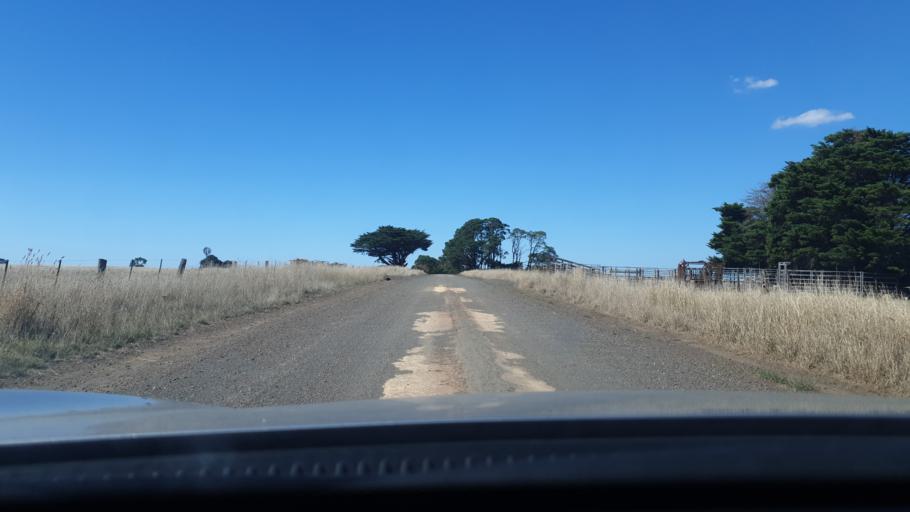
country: AU
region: Victoria
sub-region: Warrnambool
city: Warrnambool
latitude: -38.1649
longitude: 142.3844
